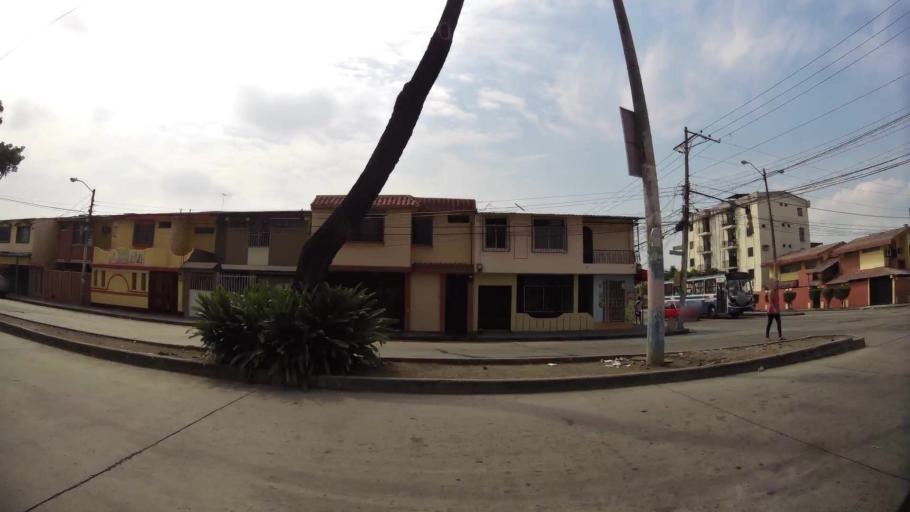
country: EC
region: Guayas
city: Guayaquil
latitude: -2.2446
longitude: -79.9003
